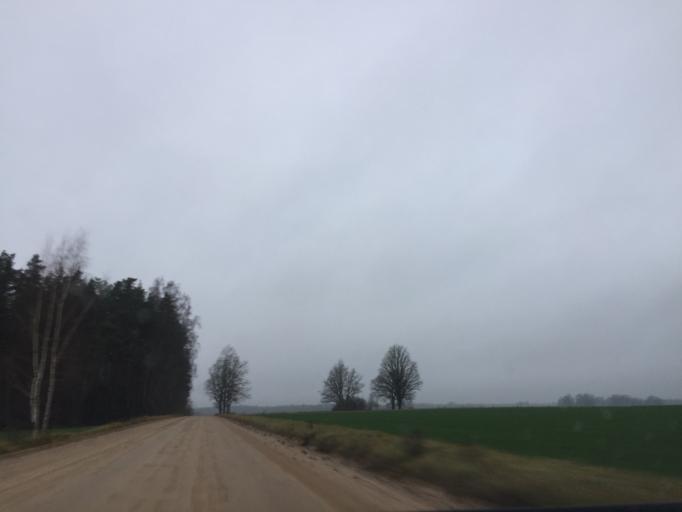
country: LV
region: Koceni
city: Koceni
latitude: 57.5420
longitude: 25.3305
